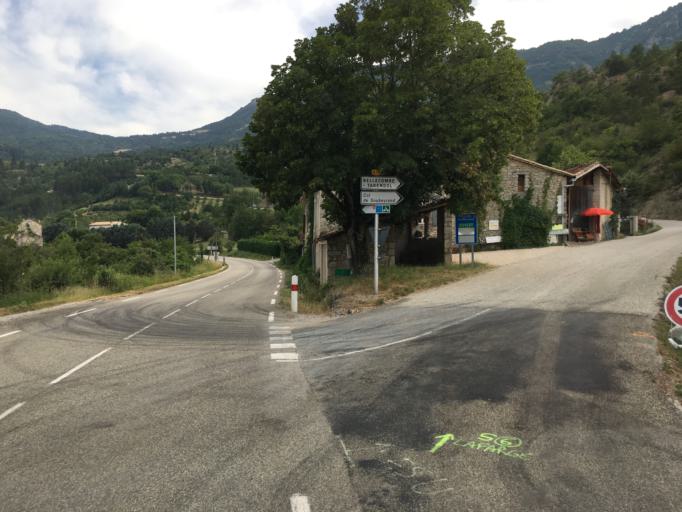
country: FR
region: Rhone-Alpes
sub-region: Departement de la Drome
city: Buis-les-Baronnies
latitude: 44.4006
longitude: 5.3501
